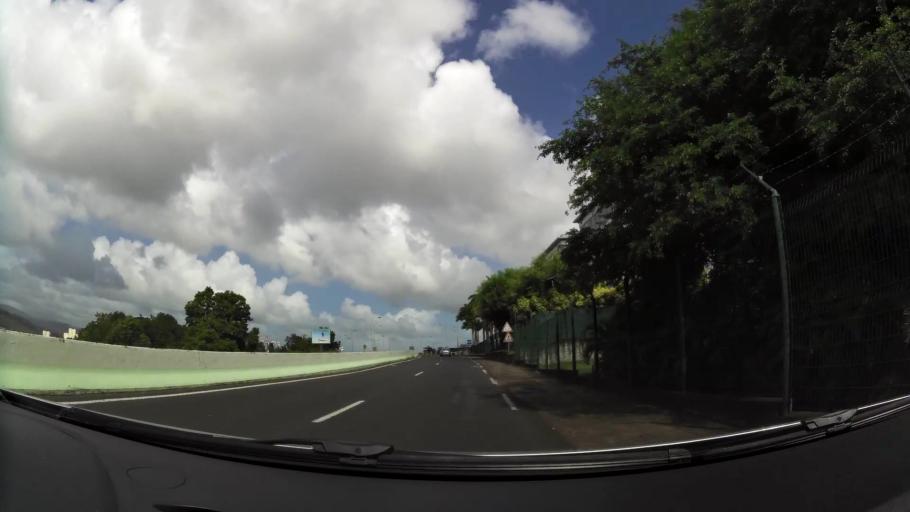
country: MQ
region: Martinique
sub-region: Martinique
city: Fort-de-France
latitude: 14.6036
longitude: -61.0434
